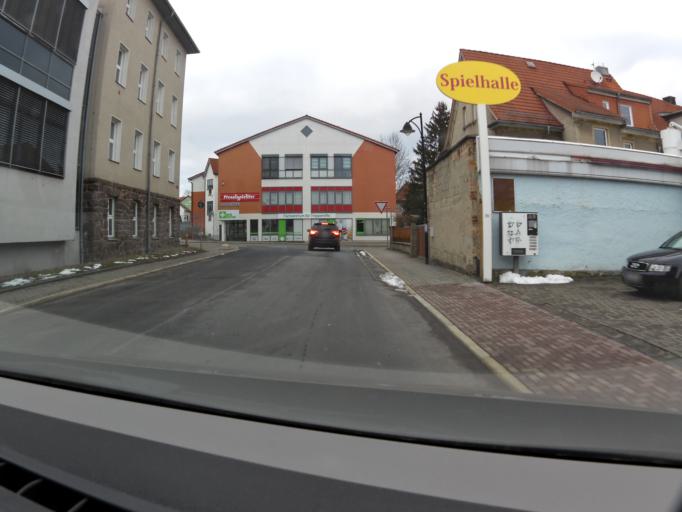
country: DE
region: Thuringia
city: Ilmenau
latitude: 50.6887
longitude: 10.9162
